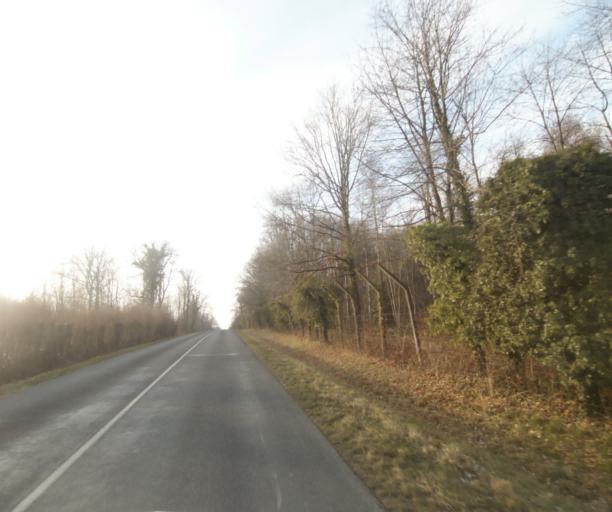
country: FR
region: Champagne-Ardenne
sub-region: Departement de la Haute-Marne
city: Chancenay
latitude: 48.6919
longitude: 4.9456
